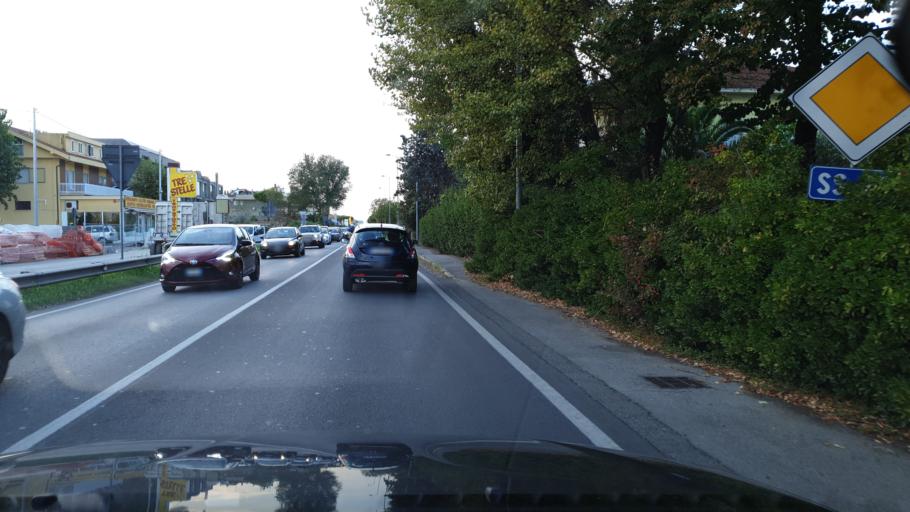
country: IT
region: Emilia-Romagna
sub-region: Provincia di Rimini
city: Rivazzurra
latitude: 44.0323
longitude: 12.6056
